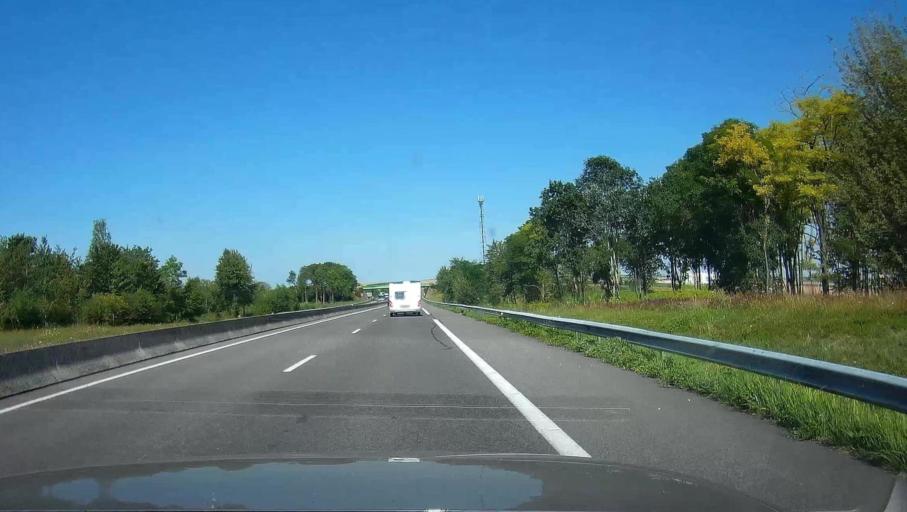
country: FR
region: Champagne-Ardenne
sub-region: Departement de l'Aube
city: Mailly-le-Camp
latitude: 48.6572
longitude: 4.1739
